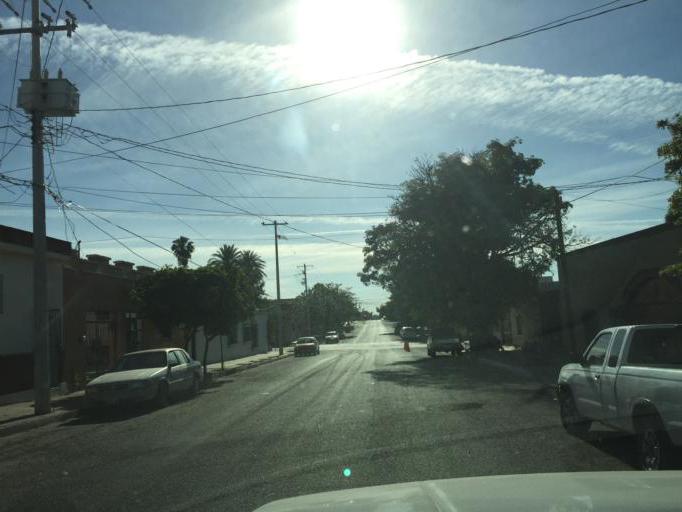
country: MX
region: Sonora
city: Navojoa
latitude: 27.0832
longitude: -109.4495
